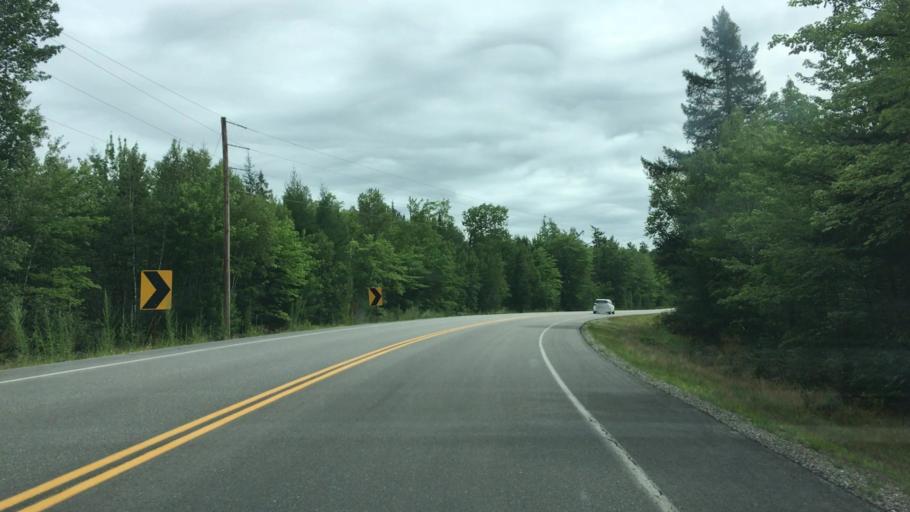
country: US
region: Maine
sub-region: Washington County
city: Machias
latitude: 45.0010
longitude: -67.5812
